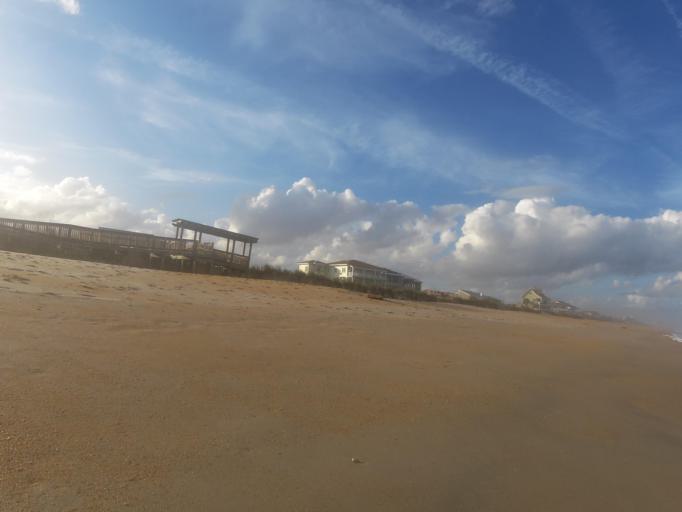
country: US
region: Florida
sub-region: Flagler County
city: Palm Coast
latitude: 29.6267
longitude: -81.1946
